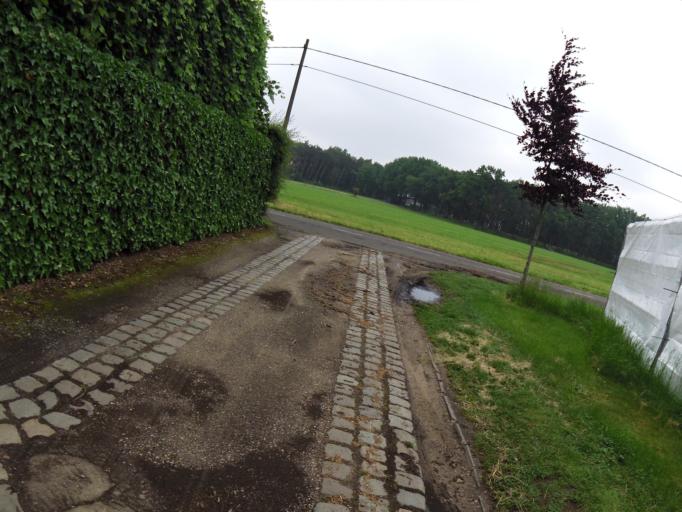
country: BE
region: Flanders
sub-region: Provincie Antwerpen
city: Geel
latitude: 51.1498
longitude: 5.0302
